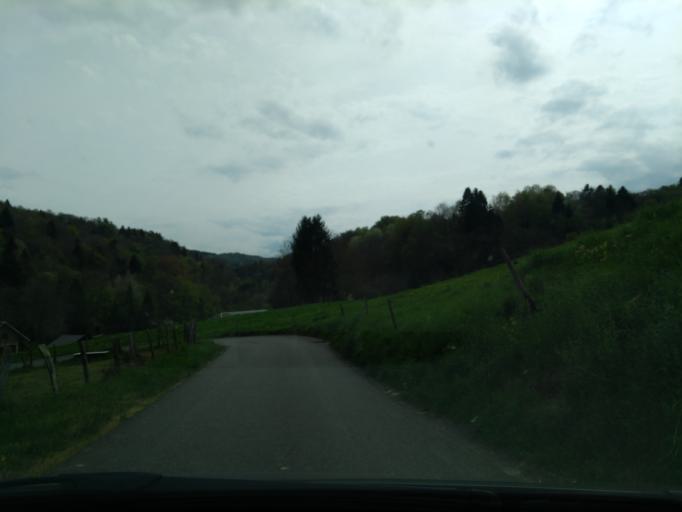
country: FR
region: Rhone-Alpes
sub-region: Departement de la Savoie
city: Chindrieux
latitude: 45.8234
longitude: 5.9022
